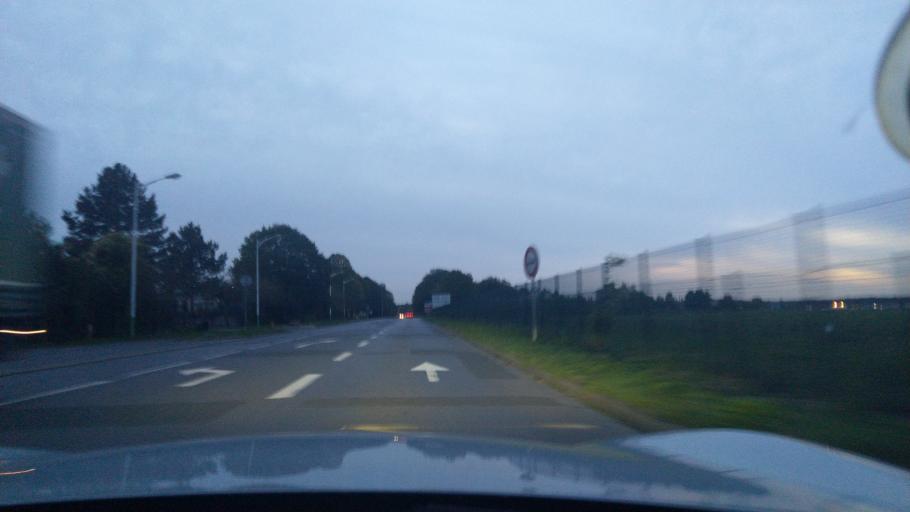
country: FR
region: Ile-de-France
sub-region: Departement de Seine-et-Marne
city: Emerainville
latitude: 48.8205
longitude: 2.6346
